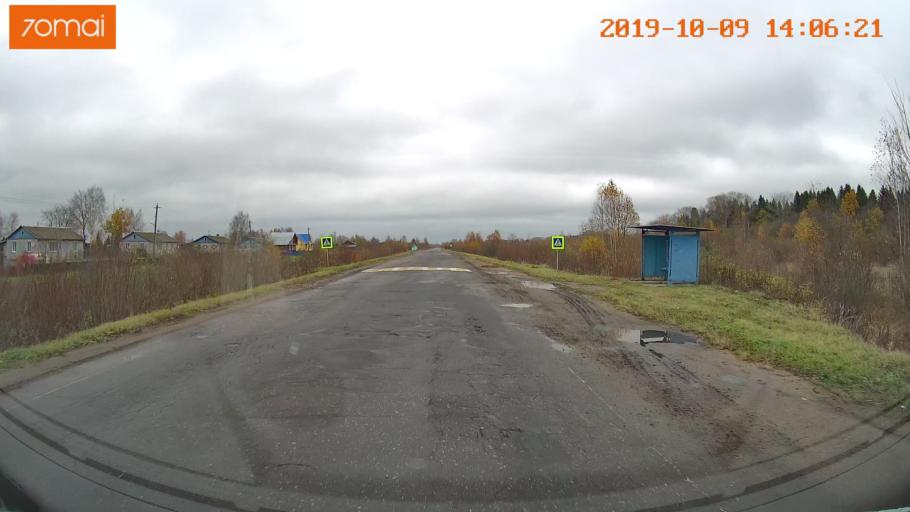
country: RU
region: Kostroma
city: Buy
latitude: 58.4643
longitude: 41.4099
